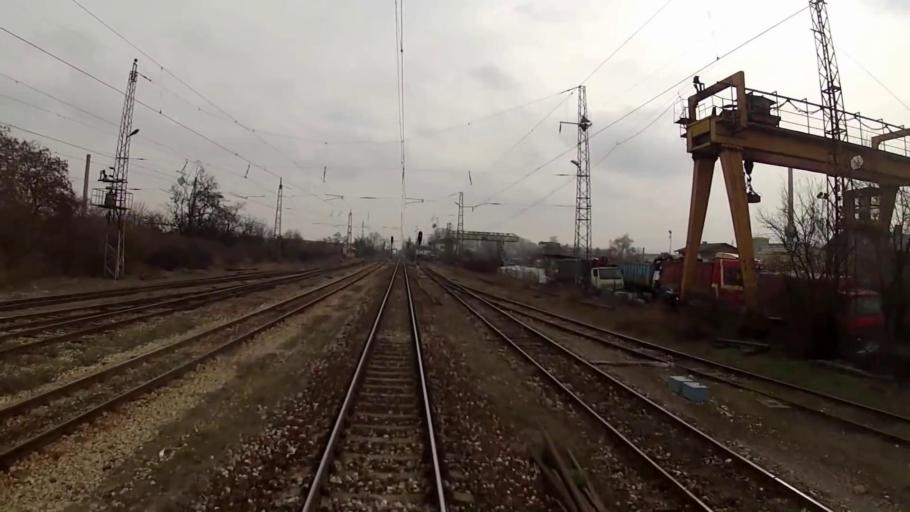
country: BG
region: Sofia-Capital
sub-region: Stolichna Obshtina
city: Sofia
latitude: 42.6546
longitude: 23.4589
